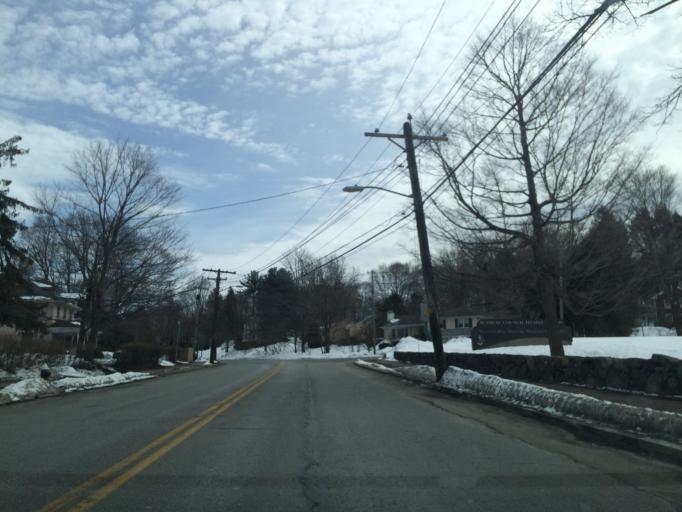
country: US
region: Massachusetts
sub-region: Middlesex County
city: Lexington
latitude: 42.4367
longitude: -71.2128
